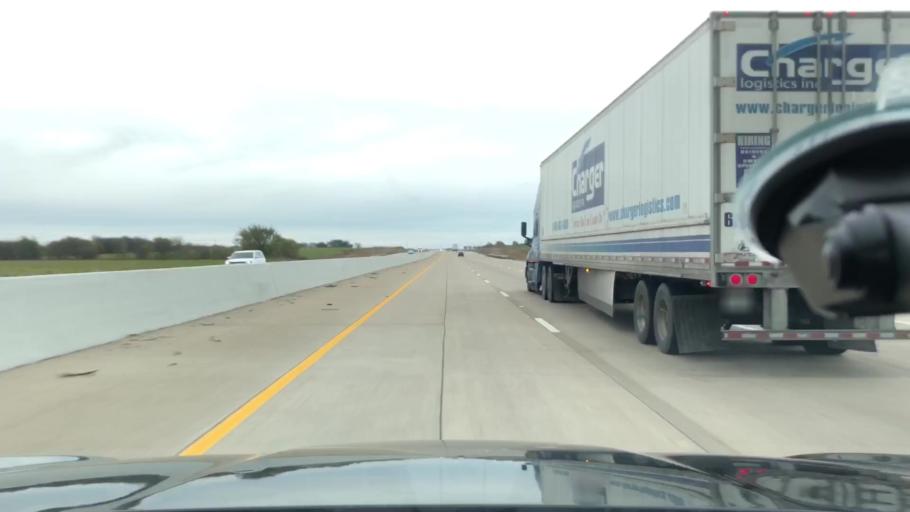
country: US
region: Texas
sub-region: Ellis County
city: Italy
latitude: 32.1495
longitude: -96.9331
